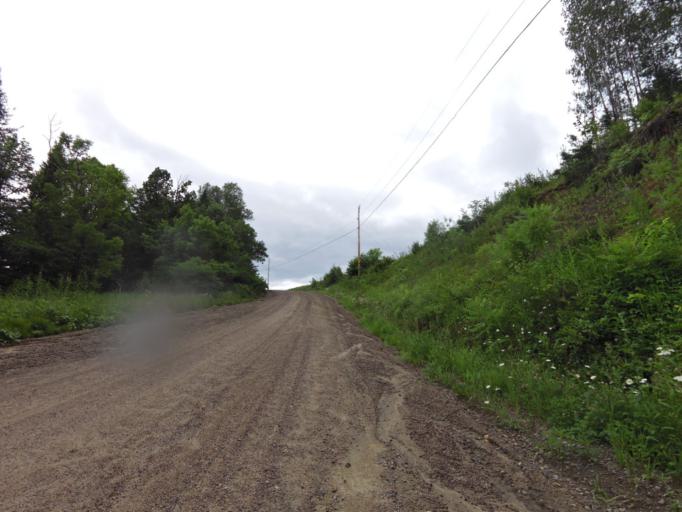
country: CA
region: Ontario
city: Hawkesbury
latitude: 45.9014
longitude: -74.6496
